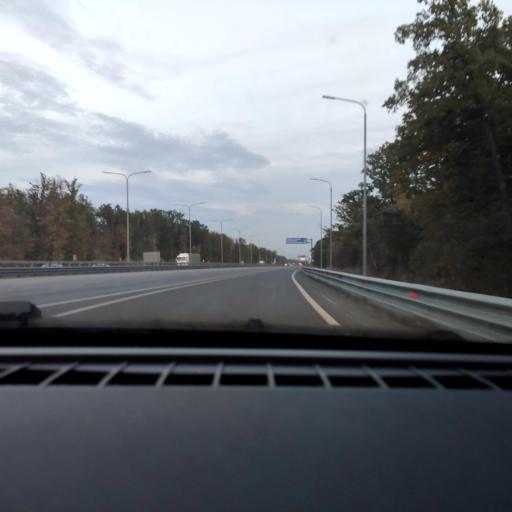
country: RU
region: Voronezj
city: Podgornoye
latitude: 51.8373
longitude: 39.2221
